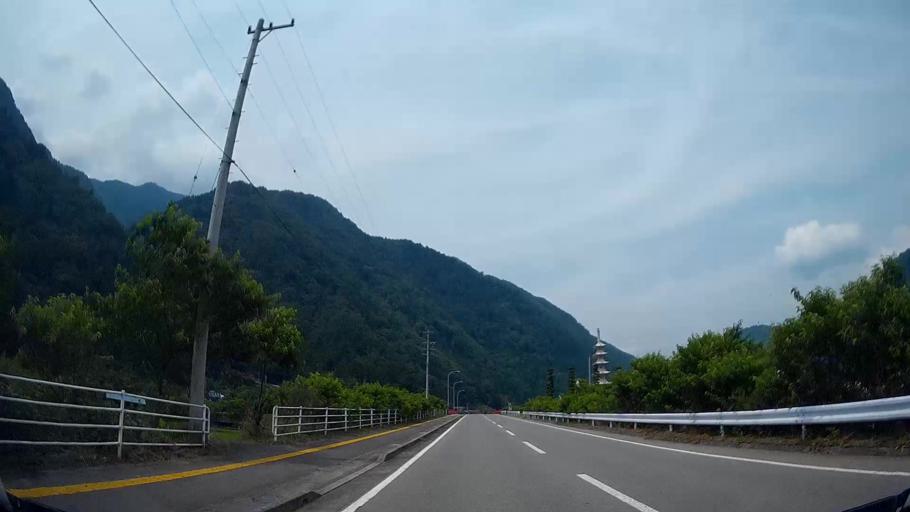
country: JP
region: Nagano
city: Iida
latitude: 35.3180
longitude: 137.9272
